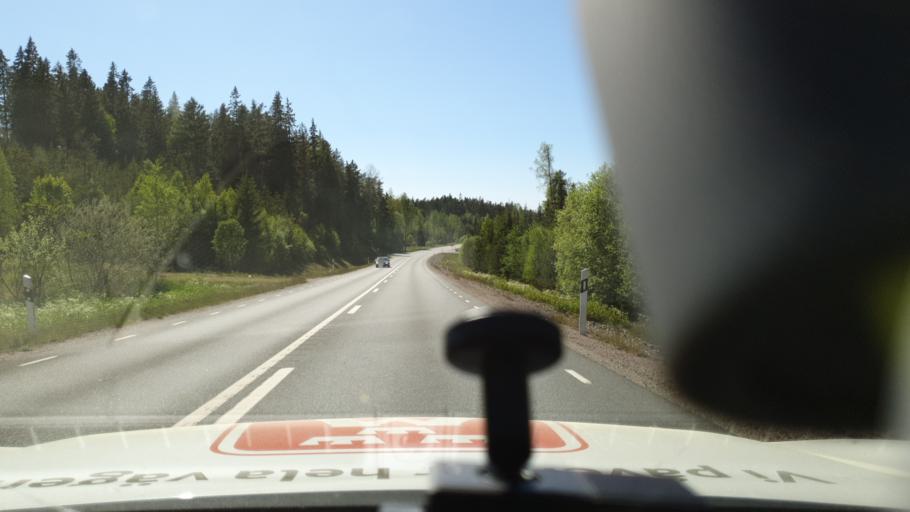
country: SE
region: Kalmar
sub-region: Hultsfreds Kommun
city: Virserum
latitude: 57.3978
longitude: 15.3694
